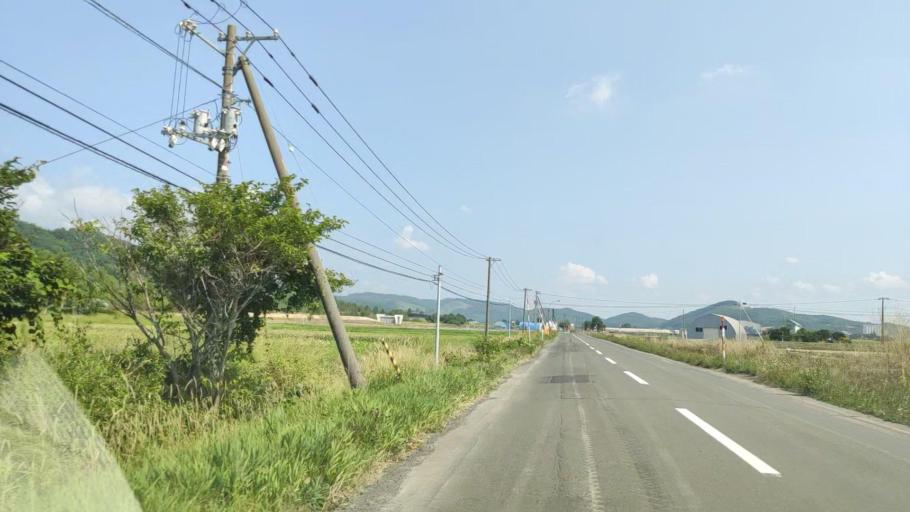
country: JP
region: Hokkaido
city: Shimo-furano
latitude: 43.3799
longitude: 142.3909
